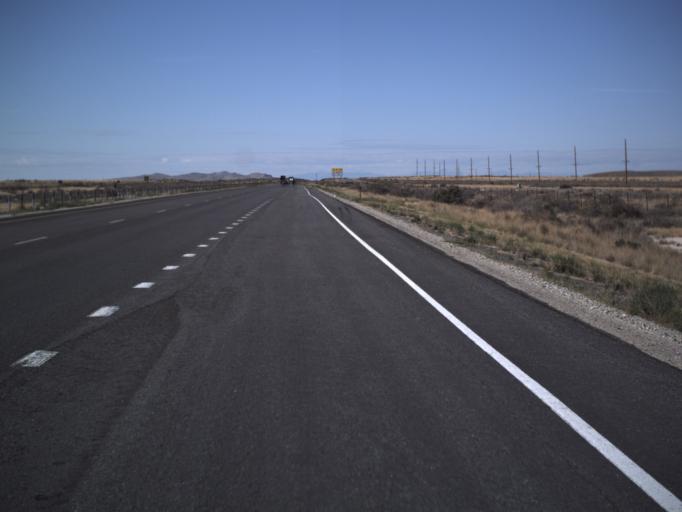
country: US
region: Utah
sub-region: Tooele County
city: Grantsville
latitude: 40.7308
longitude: -113.1199
